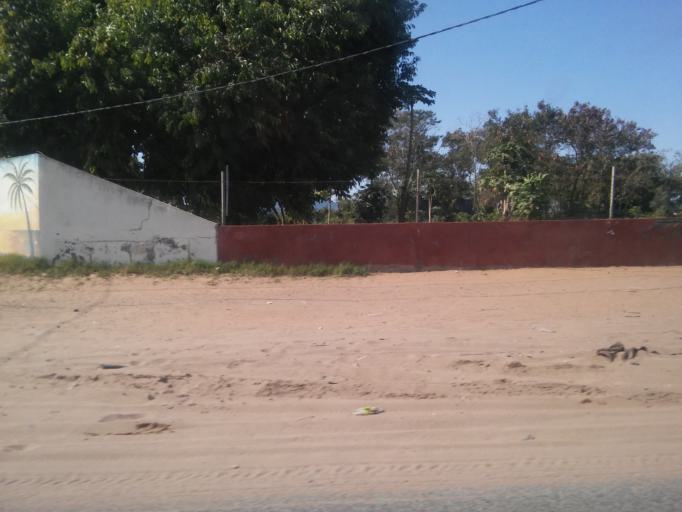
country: MZ
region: Maputo City
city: Maputo
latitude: -25.8575
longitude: 32.5671
